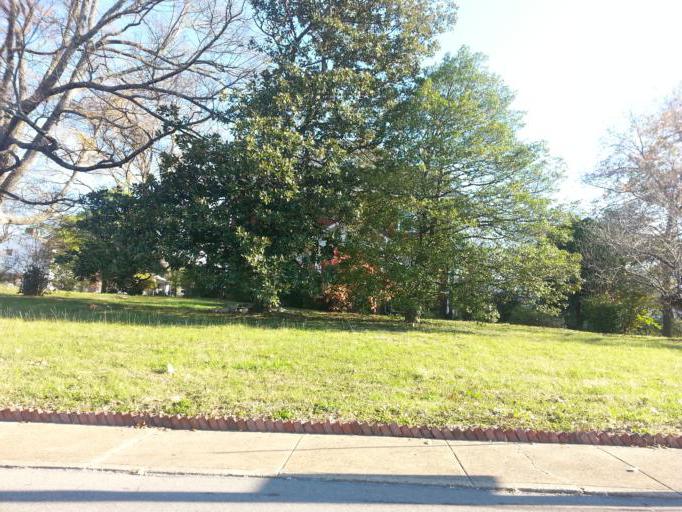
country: US
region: Tennessee
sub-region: Knox County
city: Knoxville
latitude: 35.9936
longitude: -83.9478
